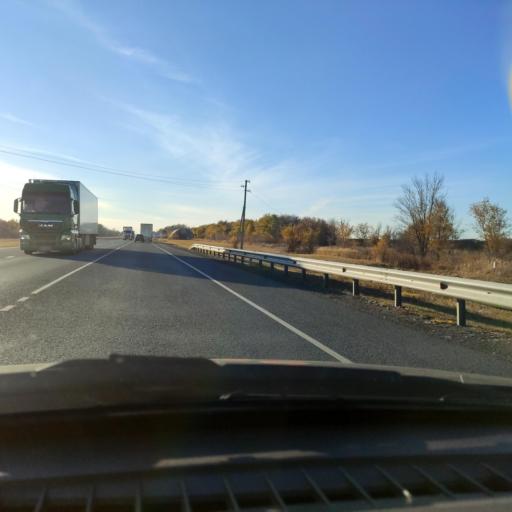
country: RU
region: Samara
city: Varlamovo
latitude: 53.1952
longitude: 48.2730
